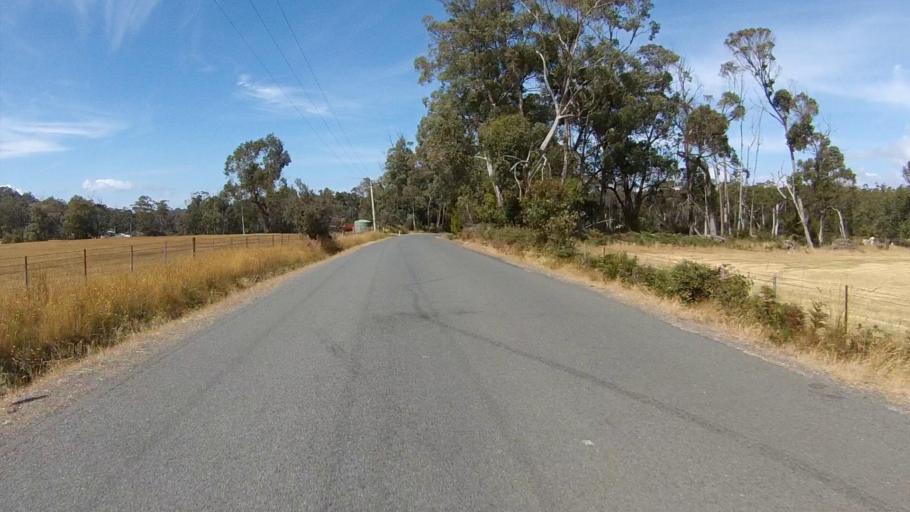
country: AU
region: Tasmania
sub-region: Huon Valley
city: Cygnet
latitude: -43.2381
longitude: 147.1249
